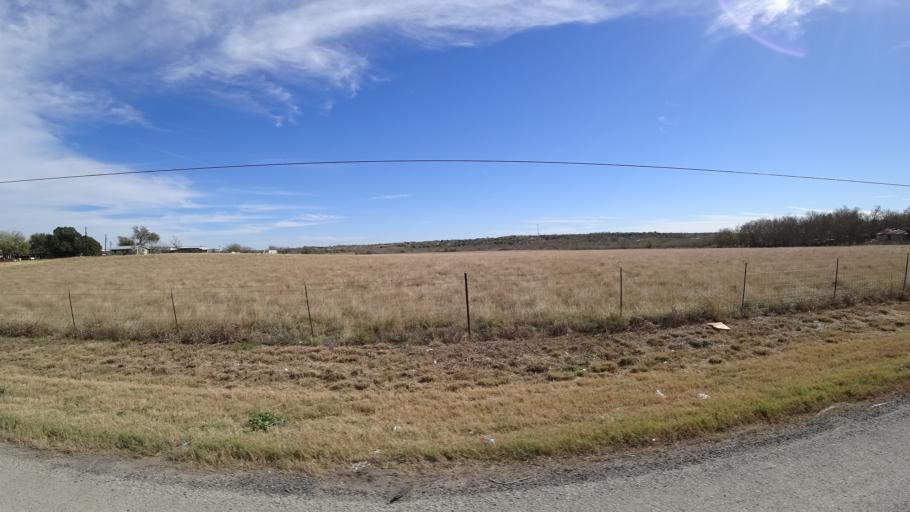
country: US
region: Texas
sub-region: Travis County
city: Onion Creek
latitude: 30.1230
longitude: -97.7139
